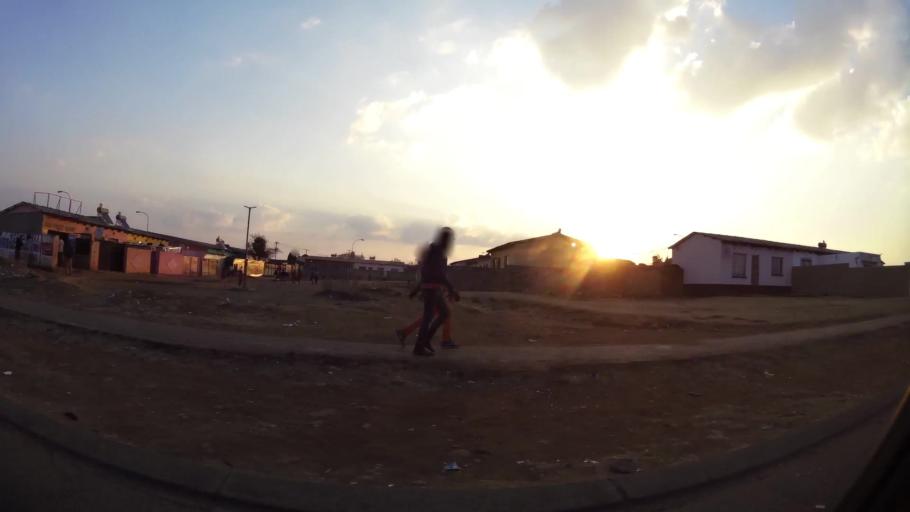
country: ZA
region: Gauteng
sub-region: City of Johannesburg Metropolitan Municipality
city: Soweto
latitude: -26.2899
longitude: 27.9003
